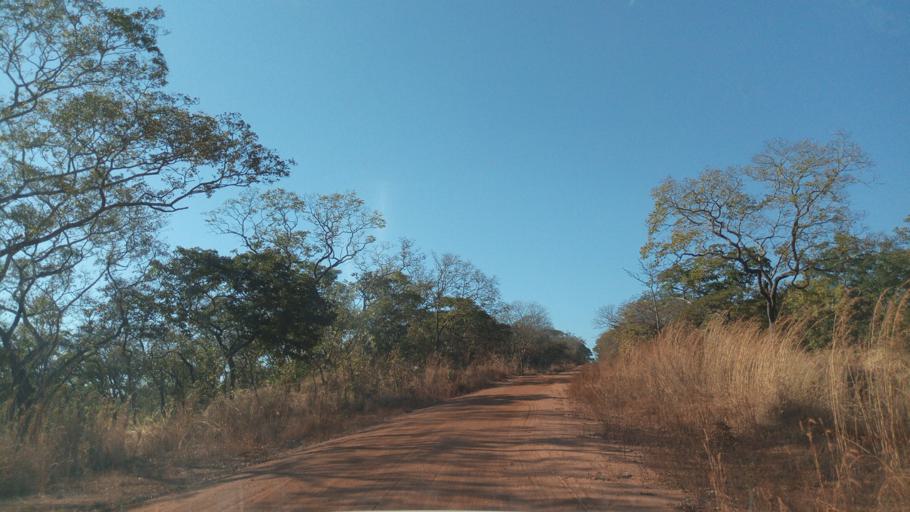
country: ZM
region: Luapula
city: Mwense
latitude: -10.5820
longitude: 28.4354
